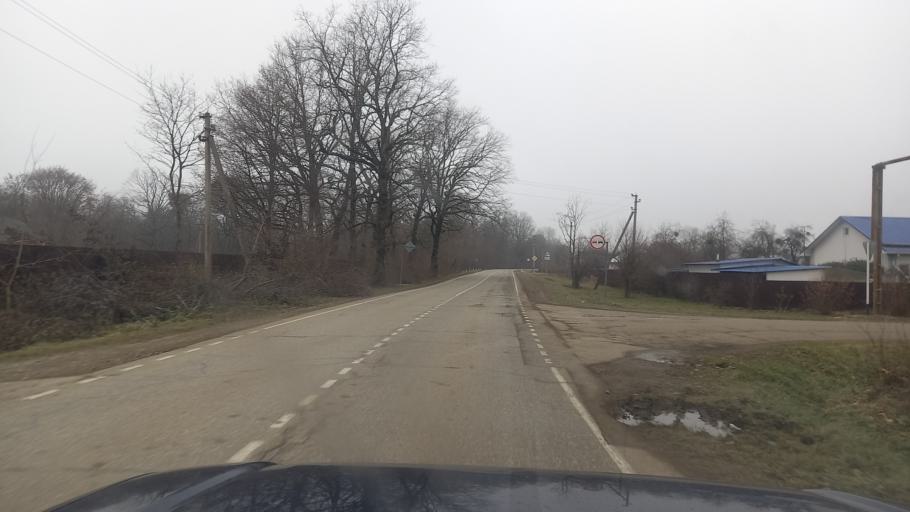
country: RU
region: Krasnodarskiy
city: Neftegorsk
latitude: 44.2930
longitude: 39.8256
